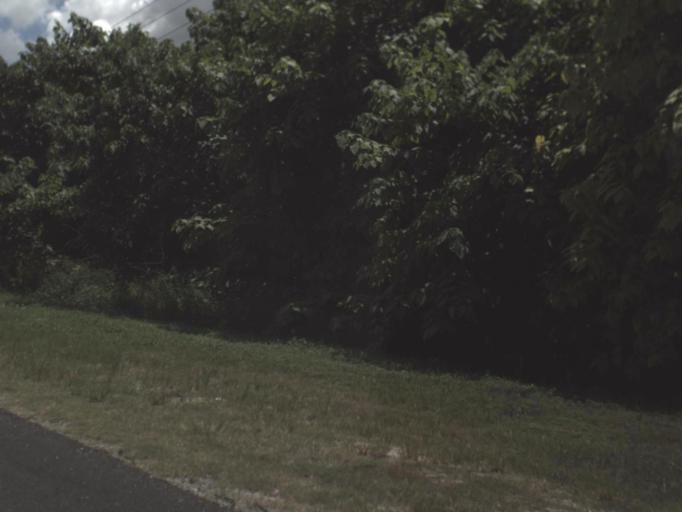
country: US
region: Florida
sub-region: Polk County
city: Lake Wales
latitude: 27.9024
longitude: -81.6091
